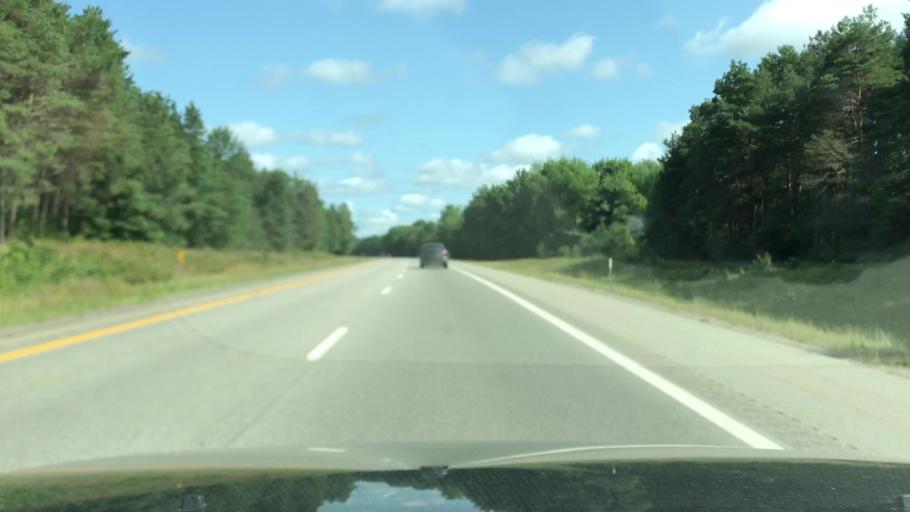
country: US
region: Michigan
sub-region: Montcalm County
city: Howard City
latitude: 43.5456
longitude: -85.4861
